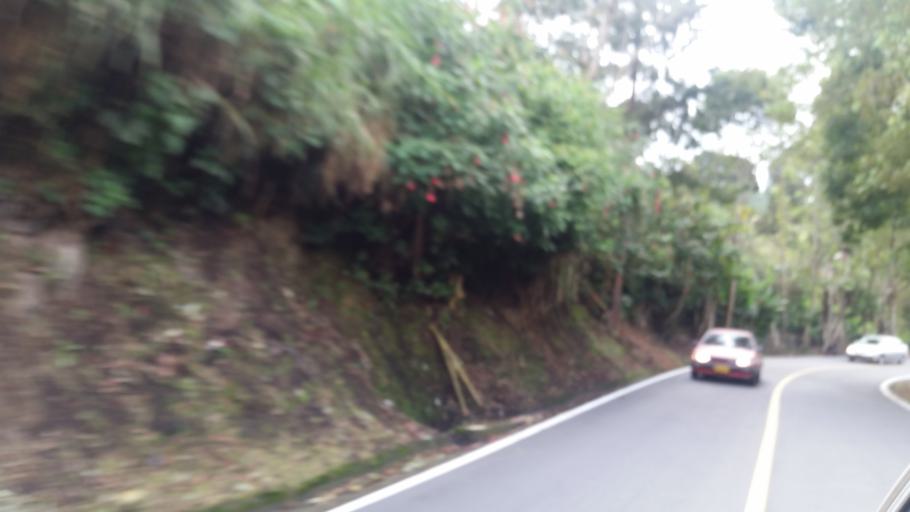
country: CO
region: Cundinamarca
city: Choachi
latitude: 4.5580
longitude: -73.9362
